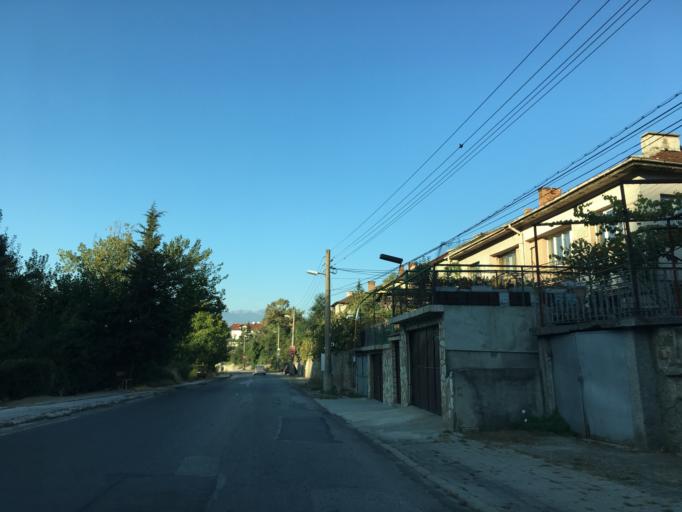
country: BG
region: Sofiya
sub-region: Obshtina Ikhtiman
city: Ikhtiman
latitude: 42.3358
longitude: 23.8791
